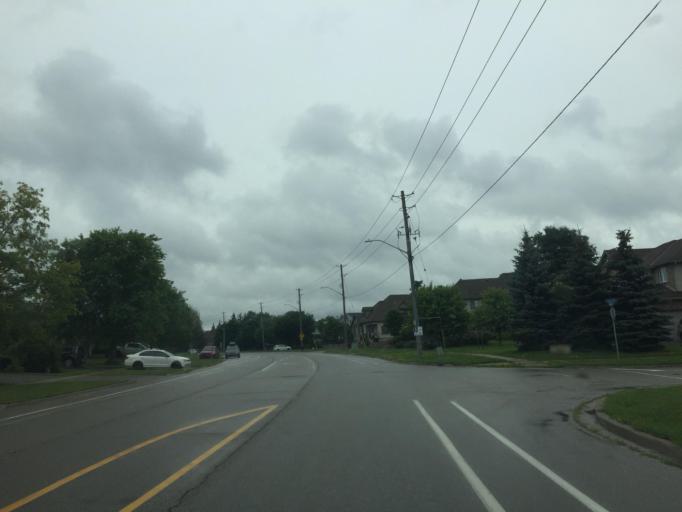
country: CA
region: Ontario
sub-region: Wellington County
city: Guelph
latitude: 43.4970
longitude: -80.2338
